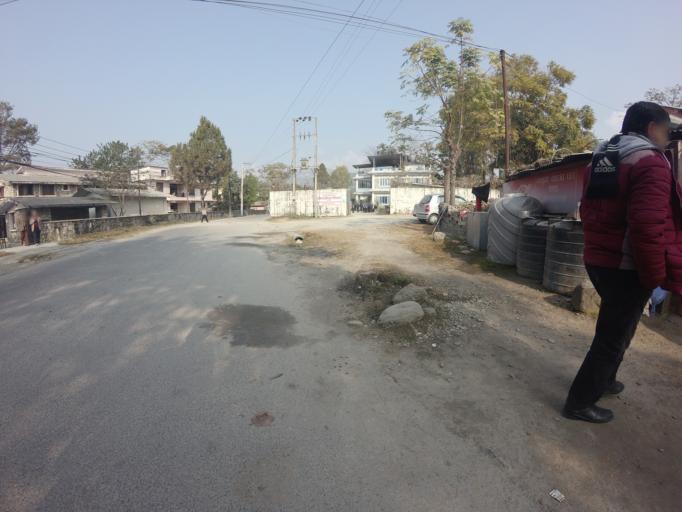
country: NP
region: Western Region
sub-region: Gandaki Zone
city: Pokhara
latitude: 28.2030
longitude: 83.9694
